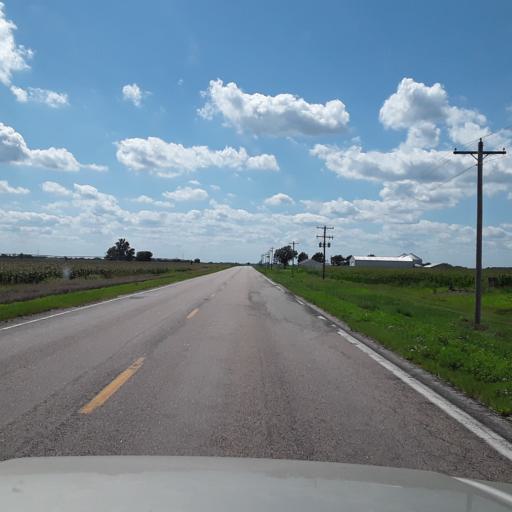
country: US
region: Nebraska
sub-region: Merrick County
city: Central City
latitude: 41.1910
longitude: -98.0312
